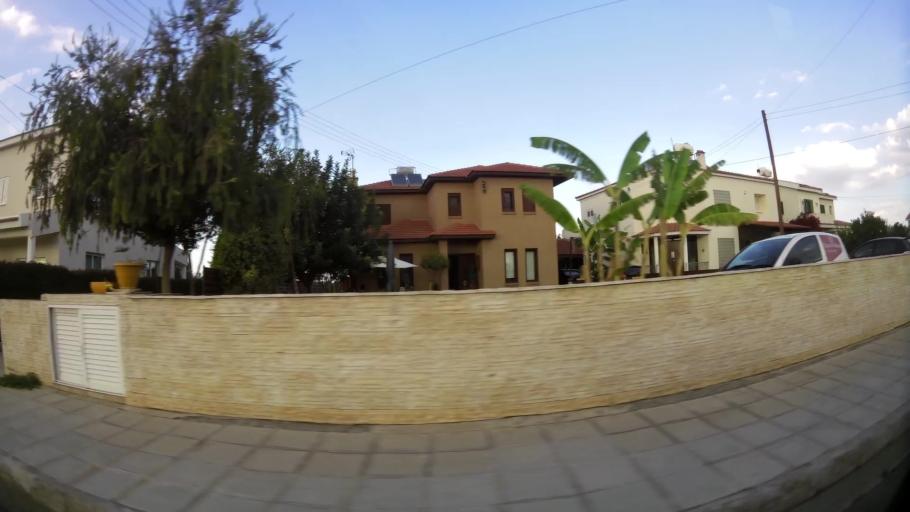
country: CY
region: Lefkosia
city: Kato Deftera
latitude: 35.1240
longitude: 33.3097
